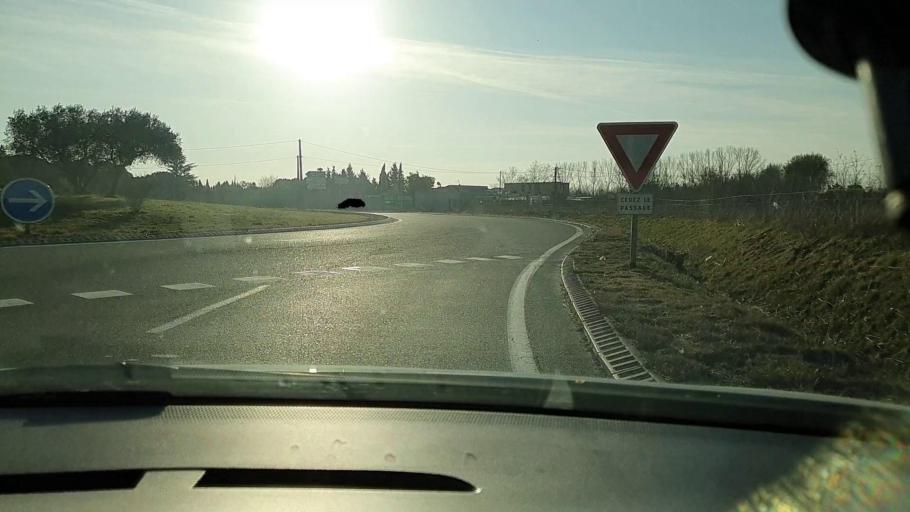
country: FR
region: Languedoc-Roussillon
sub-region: Departement du Gard
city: Manduel
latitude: 43.8290
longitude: 4.4659
